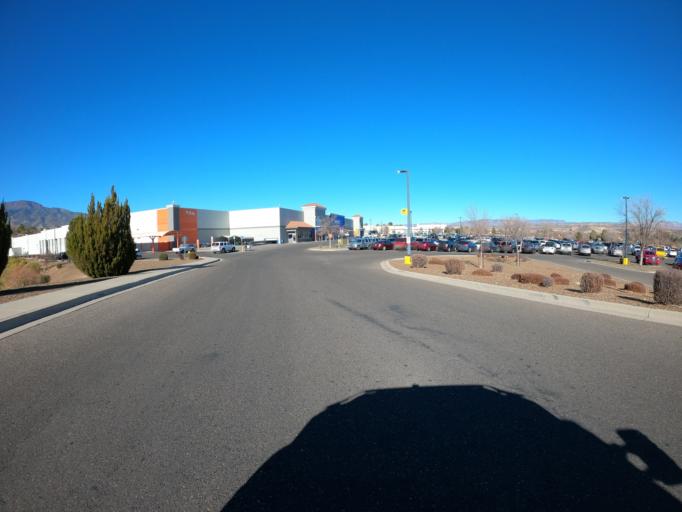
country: US
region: Arizona
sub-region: Yavapai County
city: Verde Village
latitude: 34.7123
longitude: -112.0000
